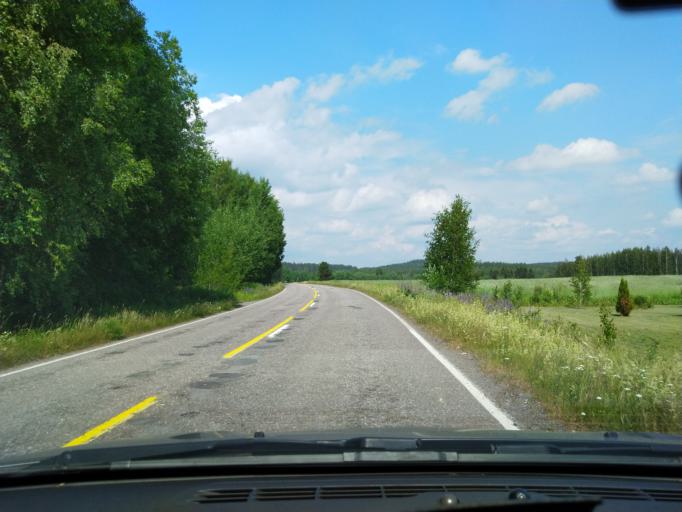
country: FI
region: Uusimaa
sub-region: Helsinki
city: Saukkola
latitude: 60.4122
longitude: 24.0696
